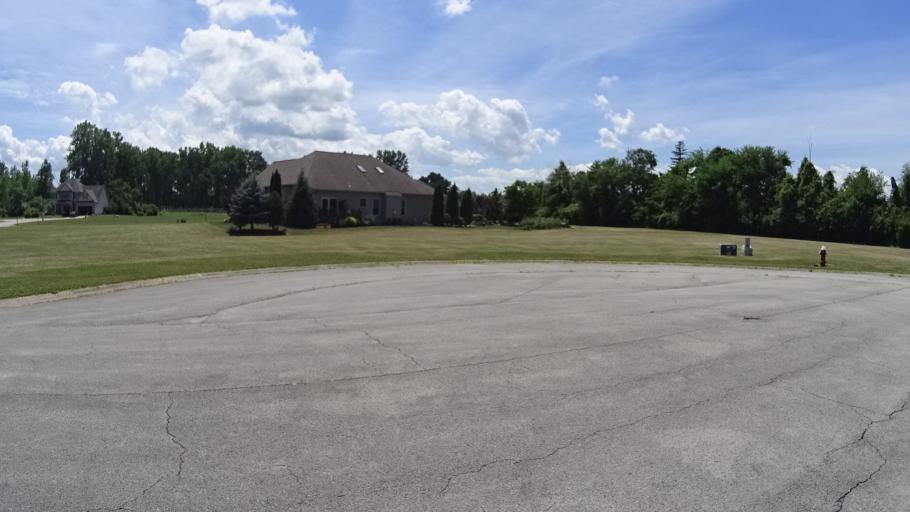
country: US
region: Ohio
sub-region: Erie County
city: Sandusky
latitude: 41.3859
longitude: -82.6637
